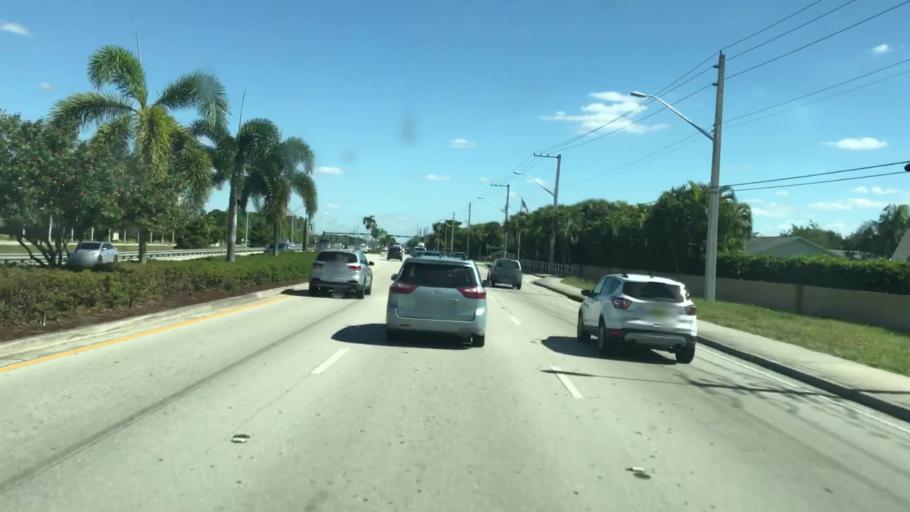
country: US
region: Florida
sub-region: Collier County
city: Naples Park
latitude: 26.2725
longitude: -81.7633
